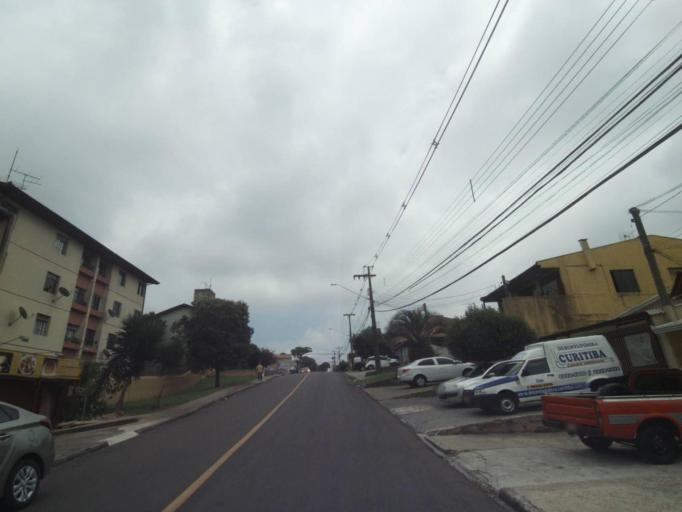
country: BR
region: Parana
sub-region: Curitiba
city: Curitiba
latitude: -25.4873
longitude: -49.3510
